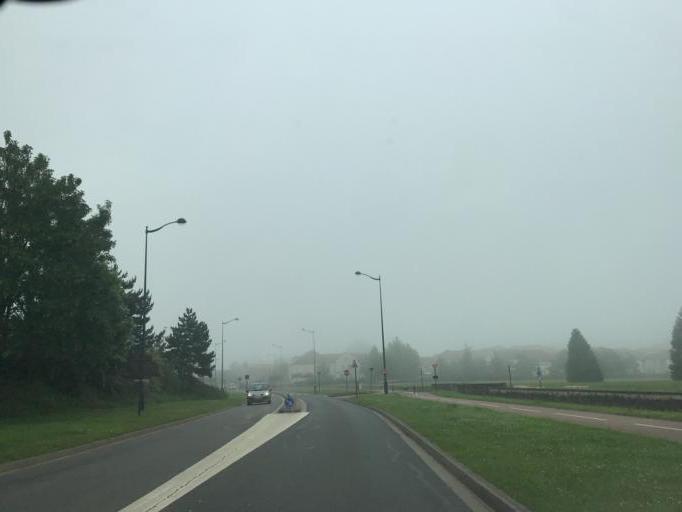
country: FR
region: Ile-de-France
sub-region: Departement de Seine-et-Marne
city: Chessy
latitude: 48.8781
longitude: 2.7623
